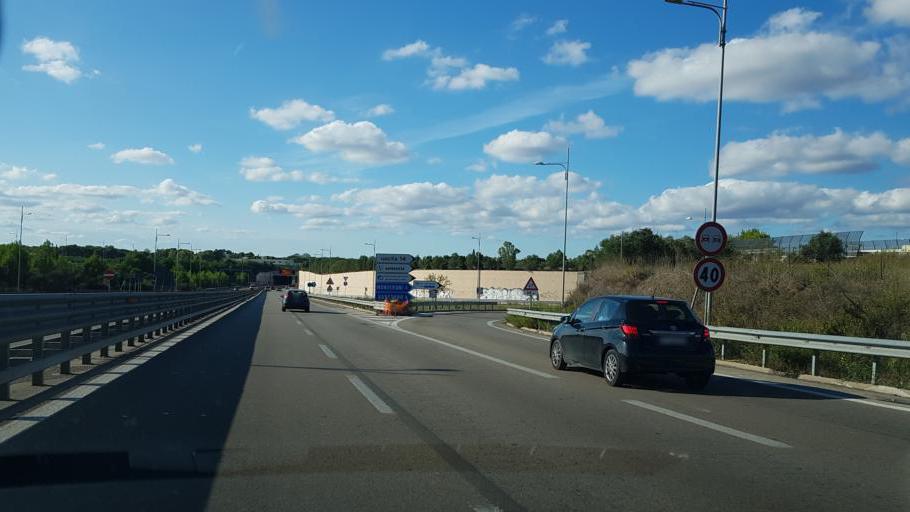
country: IT
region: Apulia
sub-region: Provincia di Lecce
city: San Pietro in Lama
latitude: 40.3330
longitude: 18.1343
